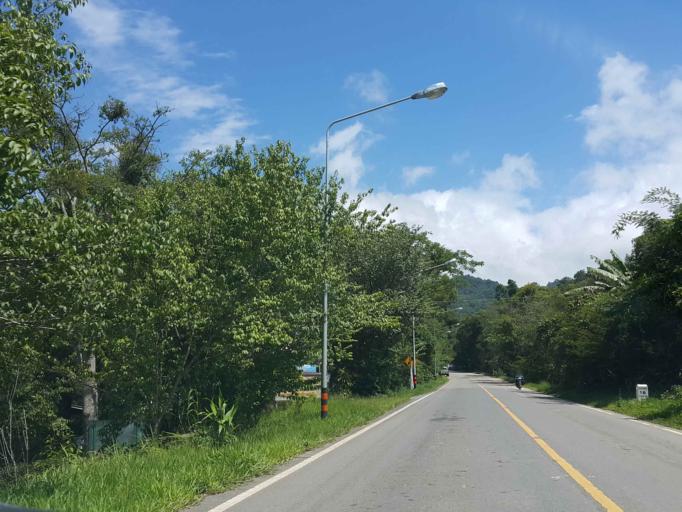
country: TH
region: Chiang Mai
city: Mae Chaem
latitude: 18.5335
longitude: 98.5218
